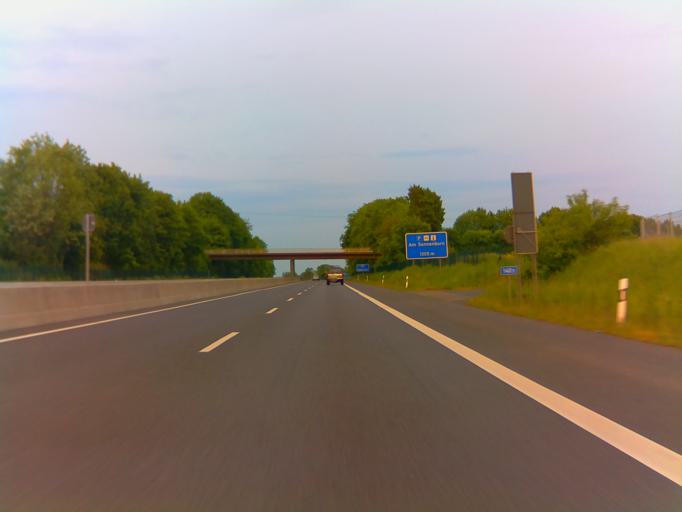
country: DE
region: Hesse
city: Gudensberg
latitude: 51.1861
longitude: 9.3784
